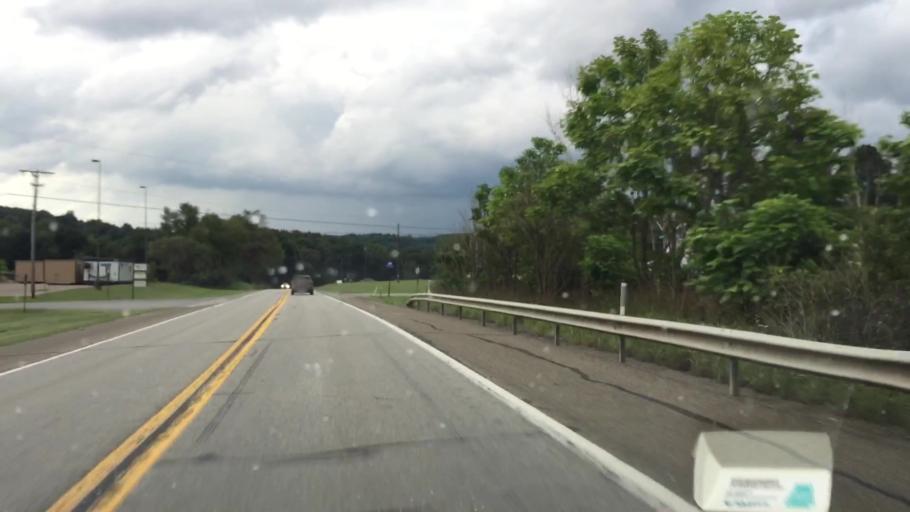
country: US
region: Pennsylvania
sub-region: Butler County
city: Evans City
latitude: 40.7859
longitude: -80.0355
